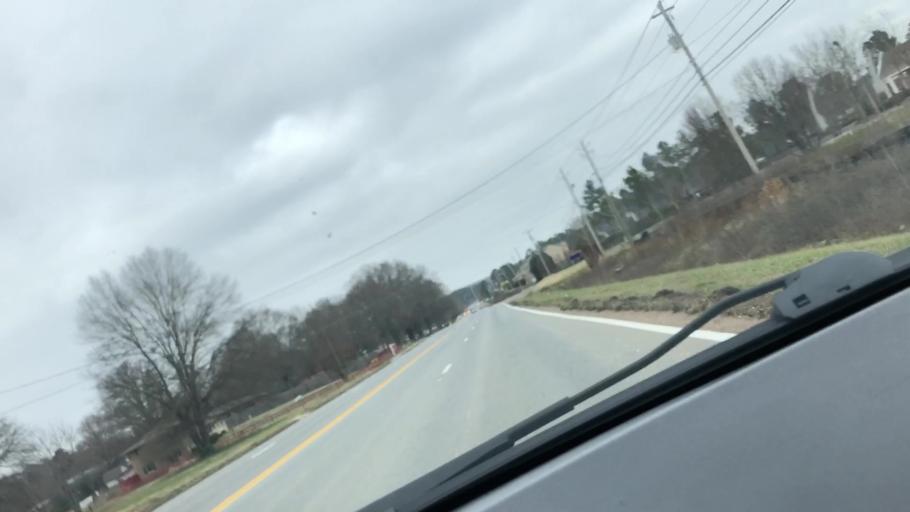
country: US
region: Georgia
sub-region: Bartow County
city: Cartersville
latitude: 34.2127
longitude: -84.8190
